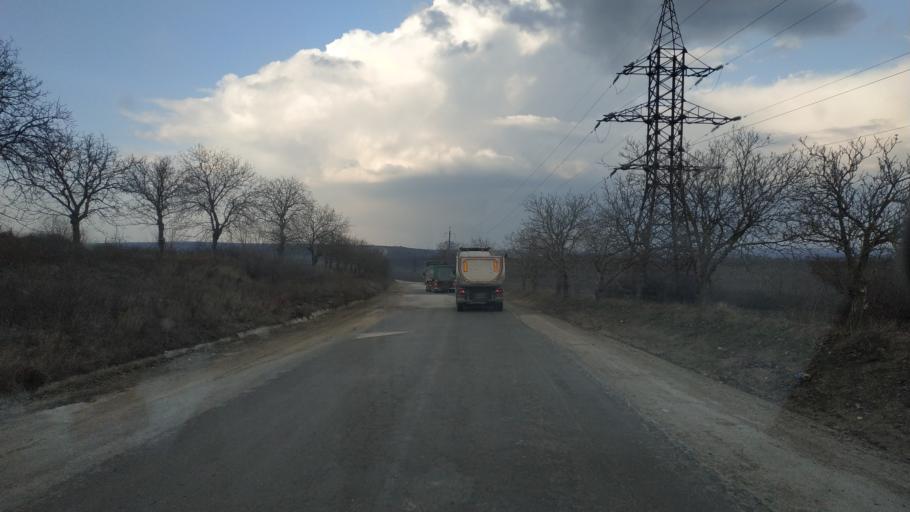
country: MD
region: Anenii Noi
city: Anenii Noi
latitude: 46.9700
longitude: 29.2851
